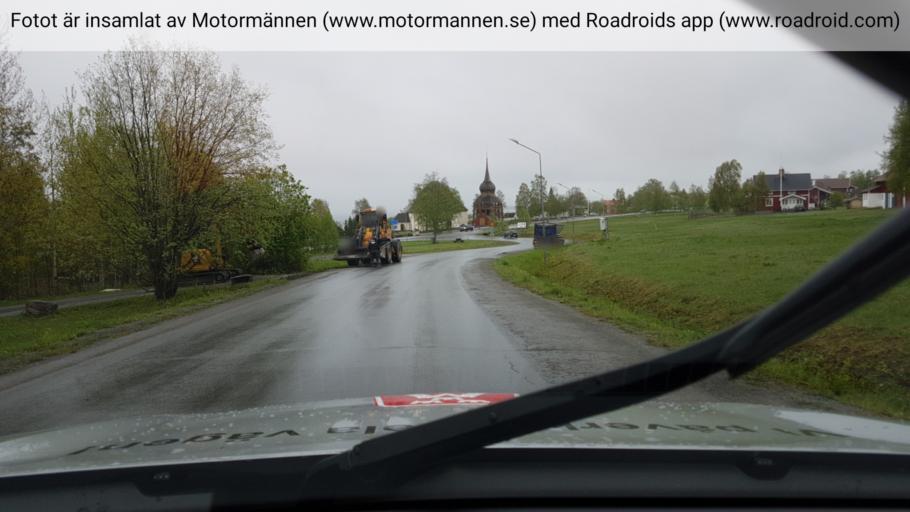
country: SE
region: Jaemtland
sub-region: Krokoms Kommun
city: Krokom
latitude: 63.1791
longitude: 14.0860
